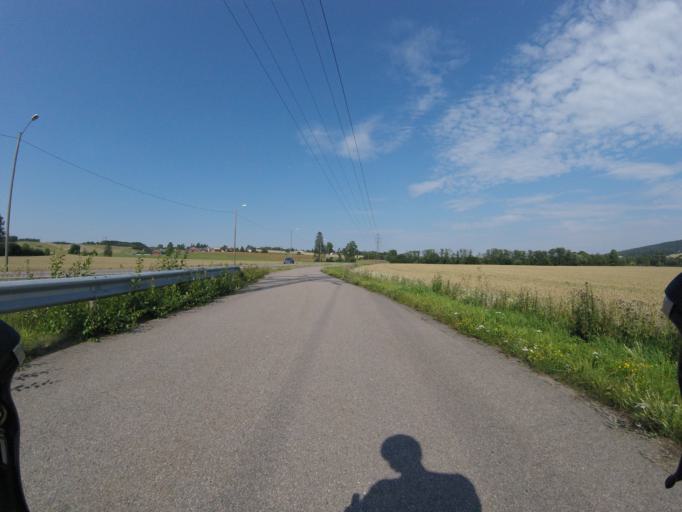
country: NO
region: Akershus
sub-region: Skedsmo
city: Leirsund
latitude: 59.9862
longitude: 11.0724
